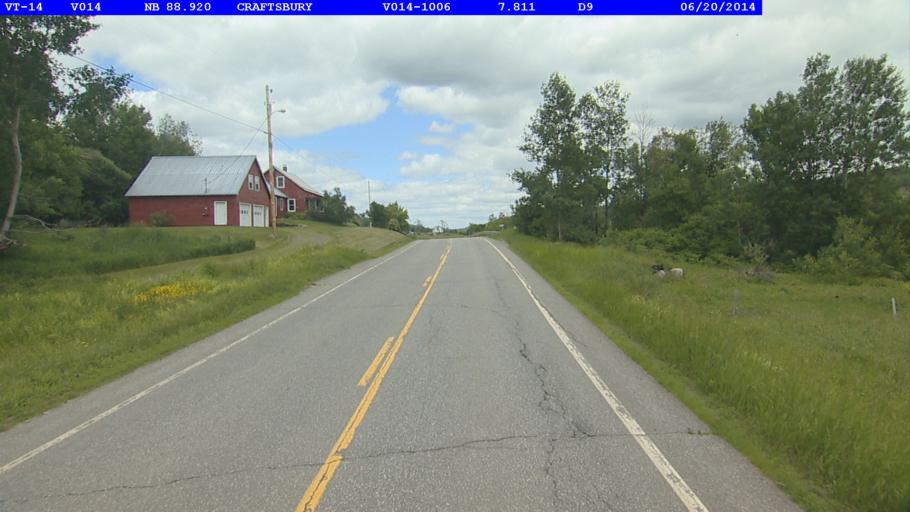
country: US
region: Vermont
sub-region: Caledonia County
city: Hardwick
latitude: 44.7012
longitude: -72.3935
